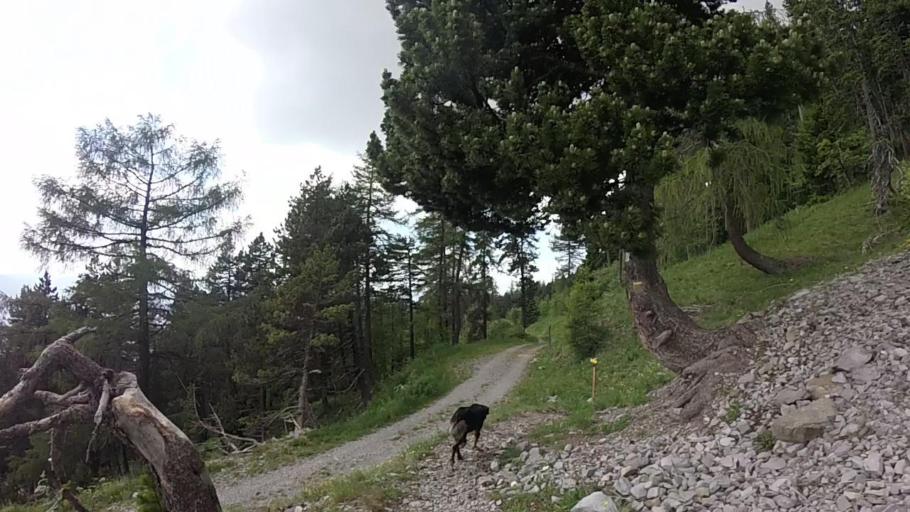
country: FR
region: Provence-Alpes-Cote d'Azur
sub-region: Departement des Alpes-de-Haute-Provence
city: Seyne-les-Alpes
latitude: 44.4006
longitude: 6.3798
